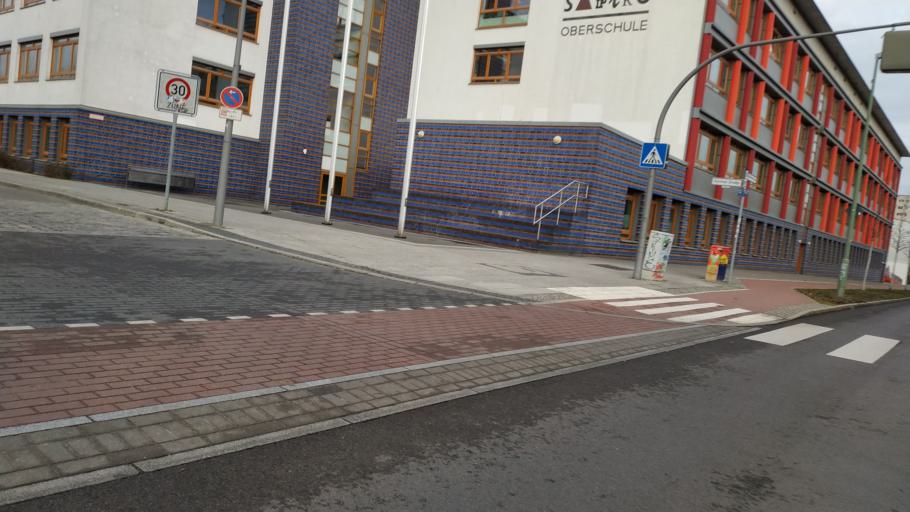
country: DE
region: Berlin
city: Hellersdorf
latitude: 52.5425
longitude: 13.5915
